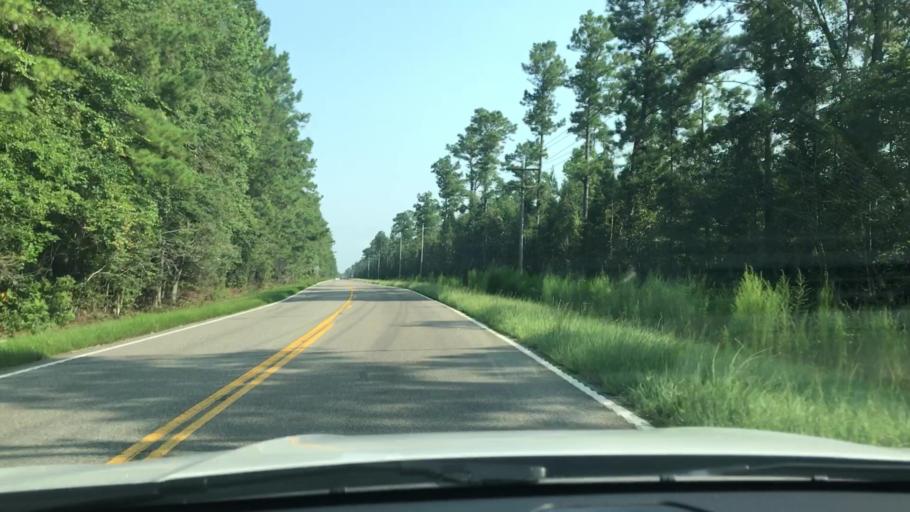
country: US
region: South Carolina
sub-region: Georgetown County
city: Georgetown
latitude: 33.4384
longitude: -79.2762
